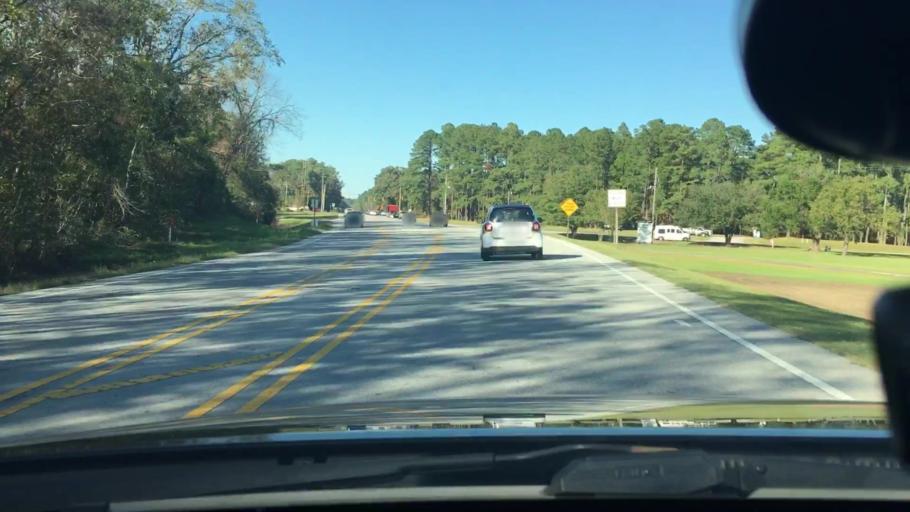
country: US
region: North Carolina
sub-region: Craven County
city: Vanceboro
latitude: 35.2139
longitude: -77.1209
